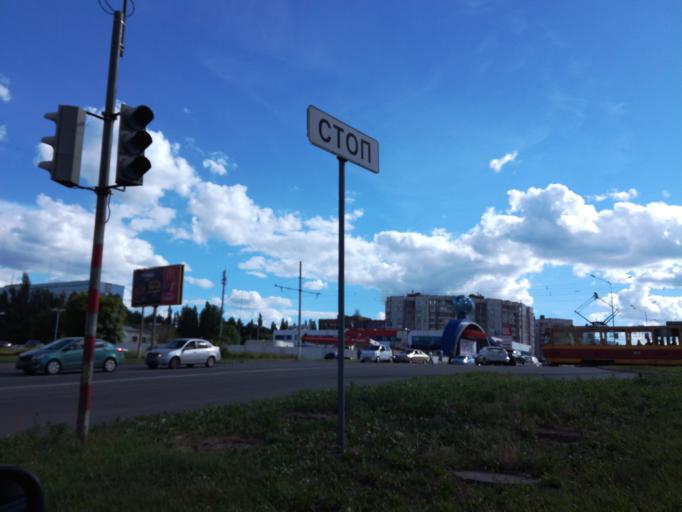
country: RU
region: Kursk
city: Kursk
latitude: 51.7414
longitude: 36.1479
